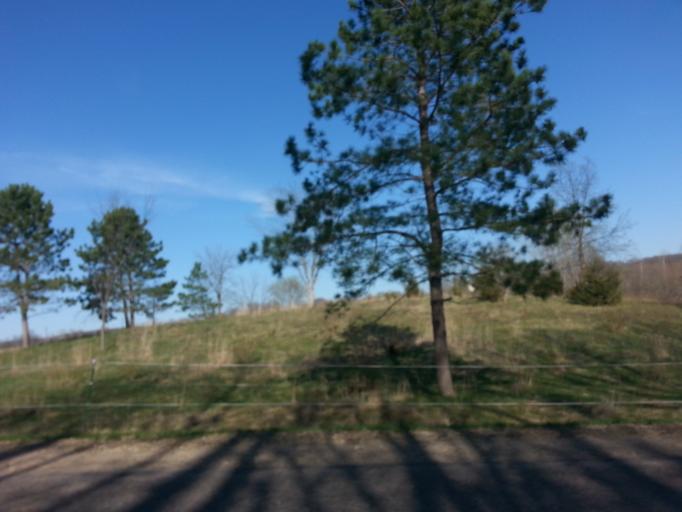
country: US
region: Wisconsin
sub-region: Pierce County
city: Ellsworth
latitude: 44.7403
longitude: -92.5779
